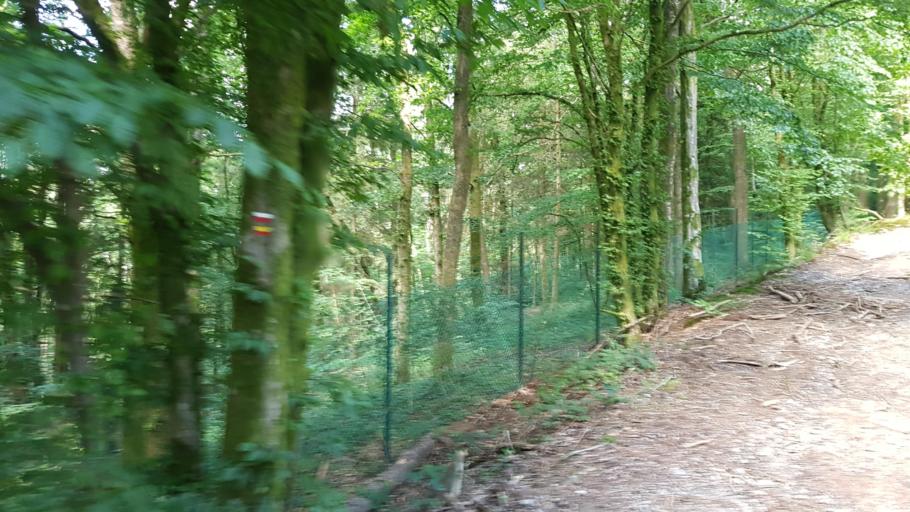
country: BE
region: Wallonia
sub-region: Province du Luxembourg
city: Bouillon
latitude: 49.7940
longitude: 5.0467
